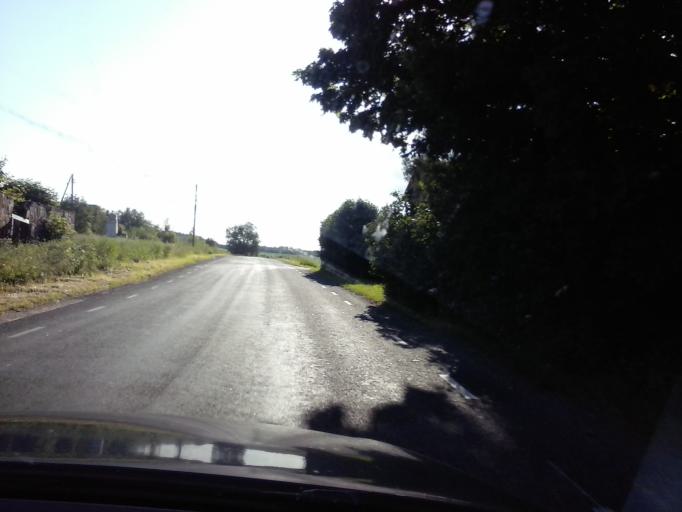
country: EE
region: Viljandimaa
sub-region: Vohma linn
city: Vohma
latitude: 58.6863
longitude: 25.6706
